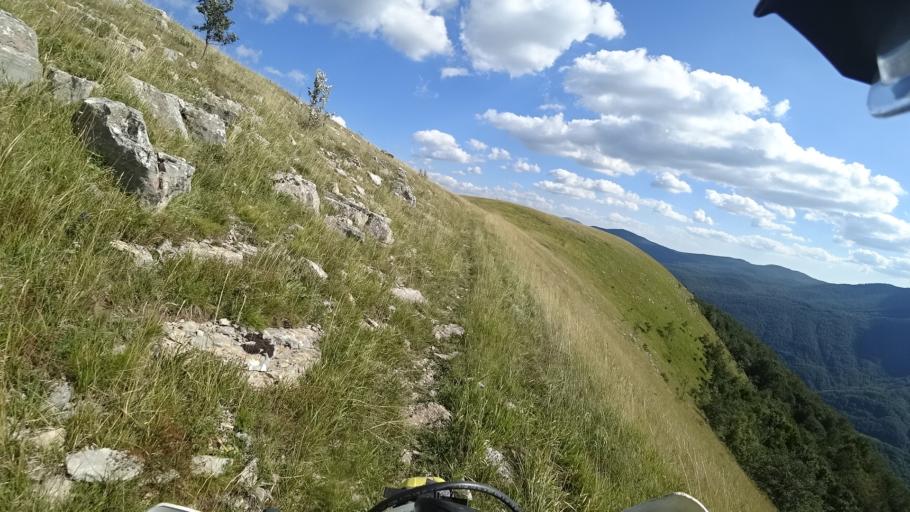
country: HR
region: Zadarska
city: Gracac
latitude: 44.3786
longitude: 16.0512
